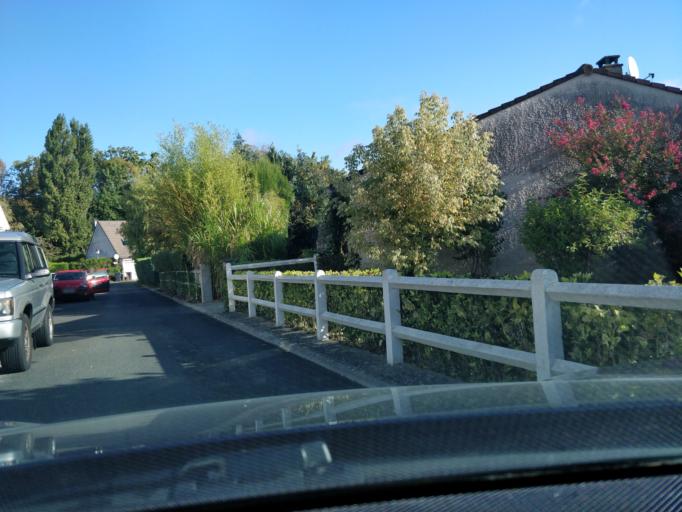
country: FR
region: Ile-de-France
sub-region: Departement de l'Essonne
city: Forges-les-Bains
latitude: 48.6279
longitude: 2.0922
